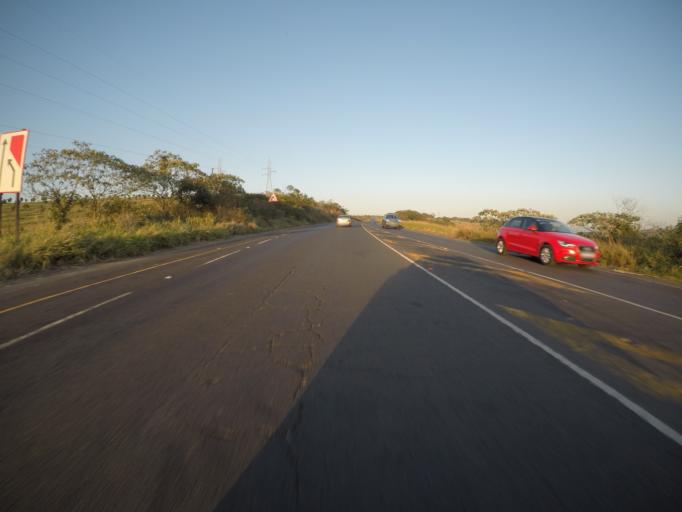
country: ZA
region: KwaZulu-Natal
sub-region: uThungulu District Municipality
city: eSikhawini
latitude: -28.8196
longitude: 31.8846
